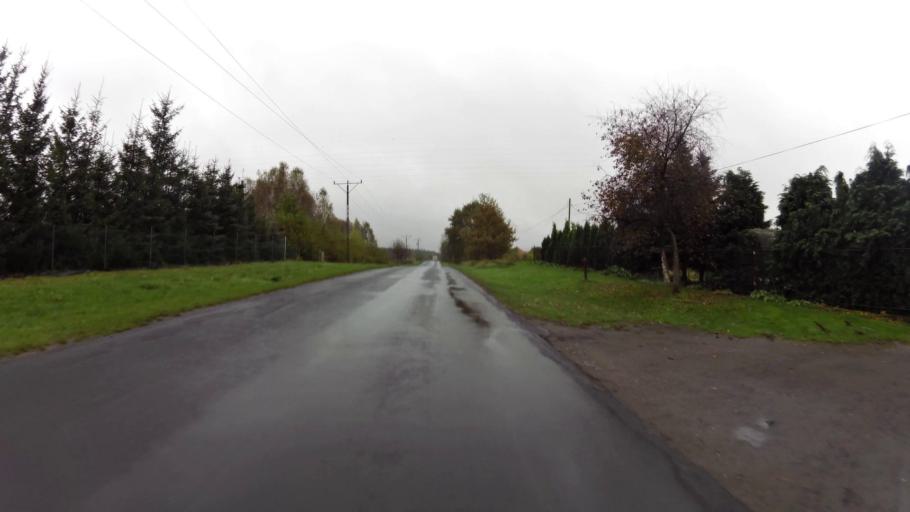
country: PL
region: West Pomeranian Voivodeship
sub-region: Powiat gryfinski
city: Gryfino
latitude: 53.2381
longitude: 14.5124
